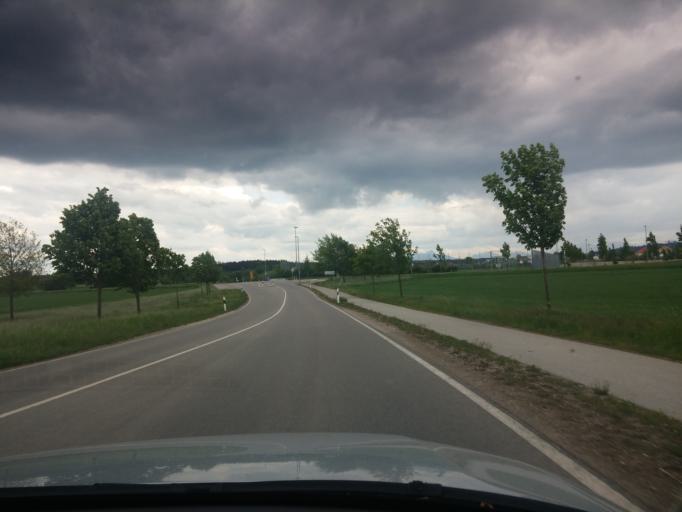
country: DE
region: Bavaria
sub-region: Upper Bavaria
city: Holzkirchen
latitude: 47.8902
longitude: 11.7040
